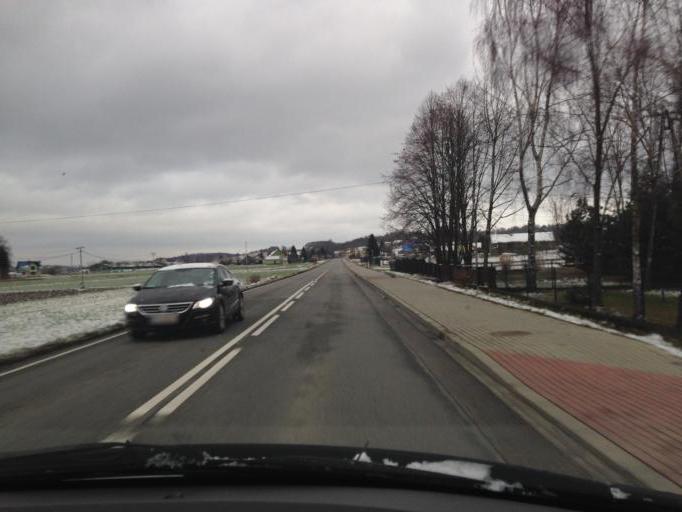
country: PL
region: Lesser Poland Voivodeship
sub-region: Powiat tarnowski
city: Zakliczyn
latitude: 49.8519
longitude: 20.8316
